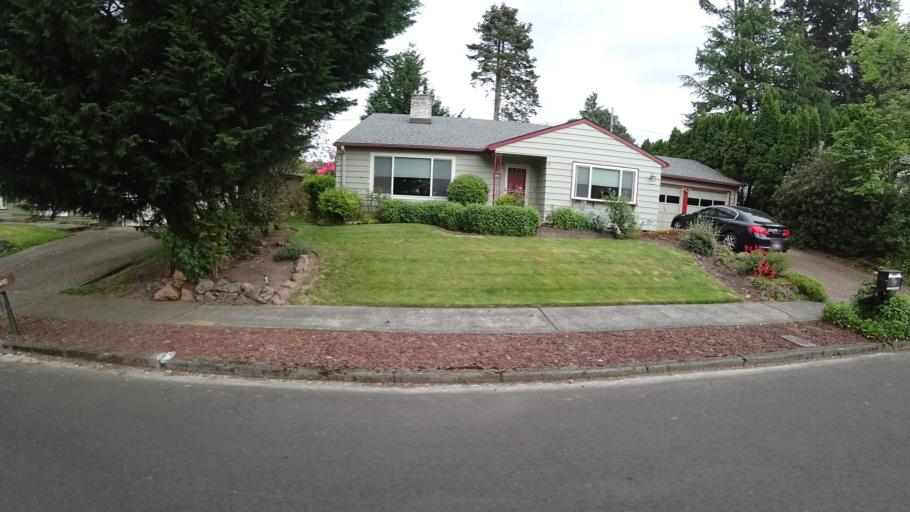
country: US
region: Oregon
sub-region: Washington County
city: Garden Home-Whitford
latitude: 45.4671
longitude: -122.7802
